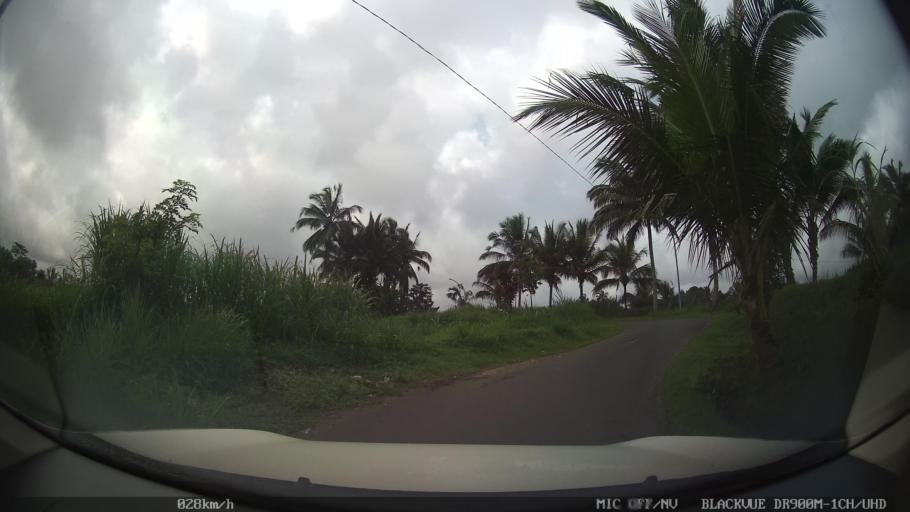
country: ID
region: Bali
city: Pemijian
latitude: -8.4397
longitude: 115.2266
